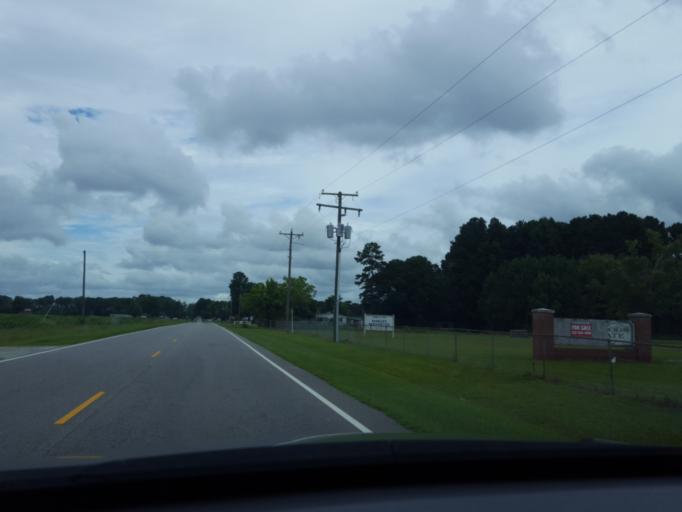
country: US
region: North Carolina
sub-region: Martin County
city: Williamston
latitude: 35.7288
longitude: -76.9791
